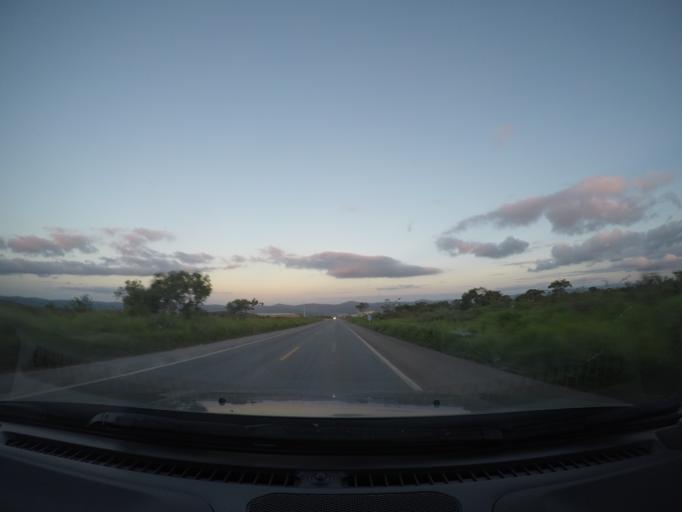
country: BR
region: Bahia
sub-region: Seabra
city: Seabra
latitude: -12.4334
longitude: -41.8153
